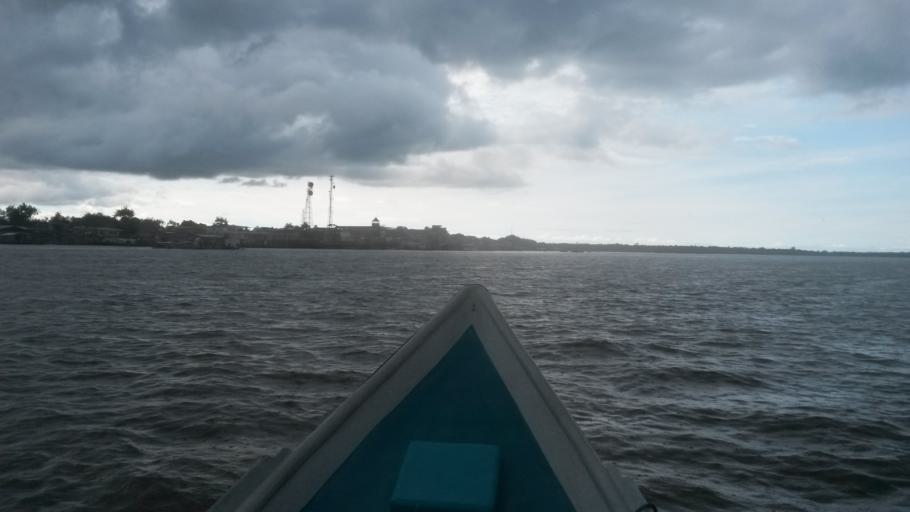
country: CO
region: Cauca
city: Guapi
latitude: 2.5672
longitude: -77.8777
